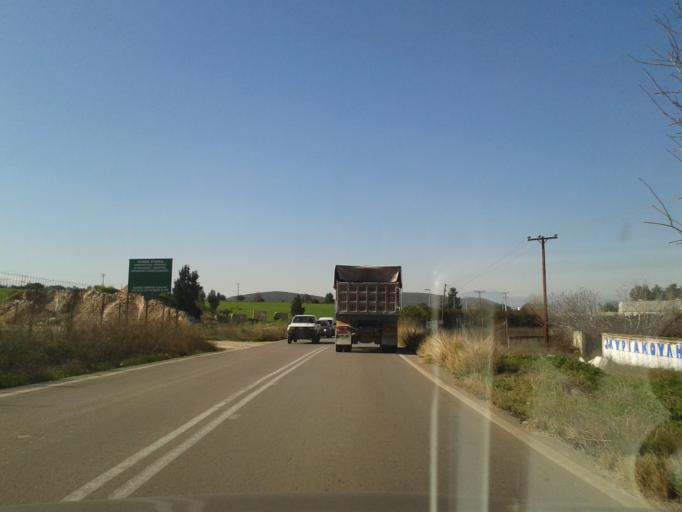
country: GR
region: Central Greece
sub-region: Nomos Voiotias
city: Arma
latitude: 38.3725
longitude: 23.4269
